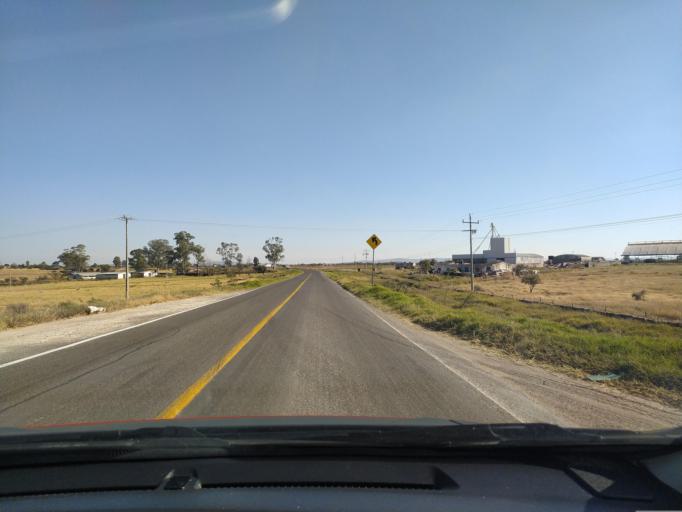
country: MX
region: Jalisco
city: Valle de Guadalupe
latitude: 21.0258
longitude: -102.5479
